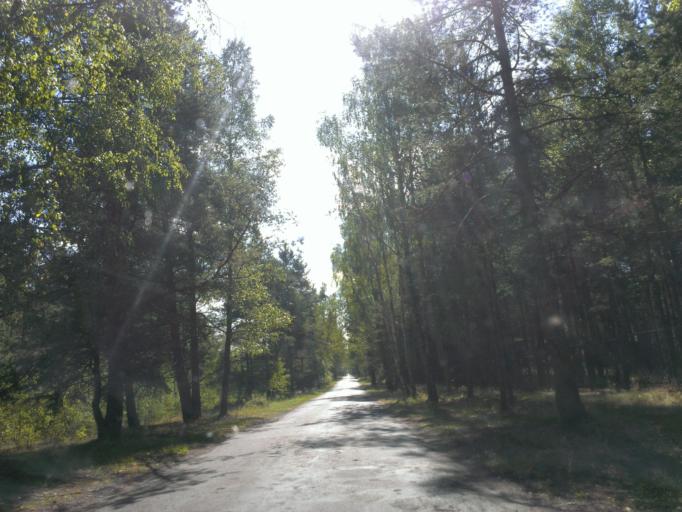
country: LV
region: Adazi
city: Adazi
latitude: 57.1126
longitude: 24.3457
